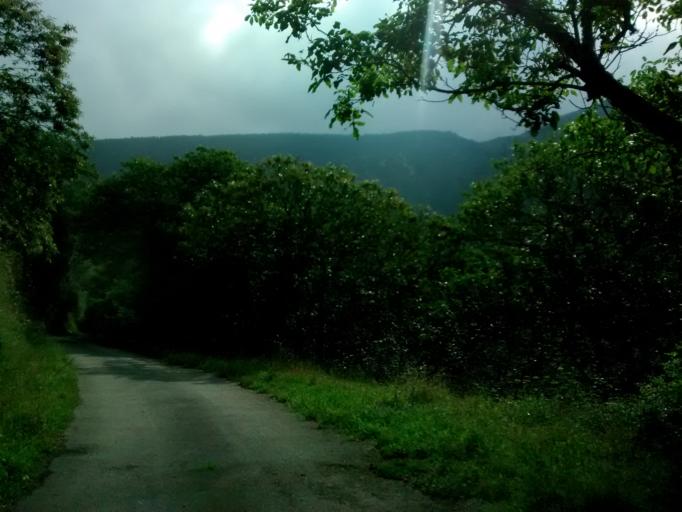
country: ES
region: Galicia
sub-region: Provincia de Ourense
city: Castro Caldelas
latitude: 42.4242
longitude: -7.3883
